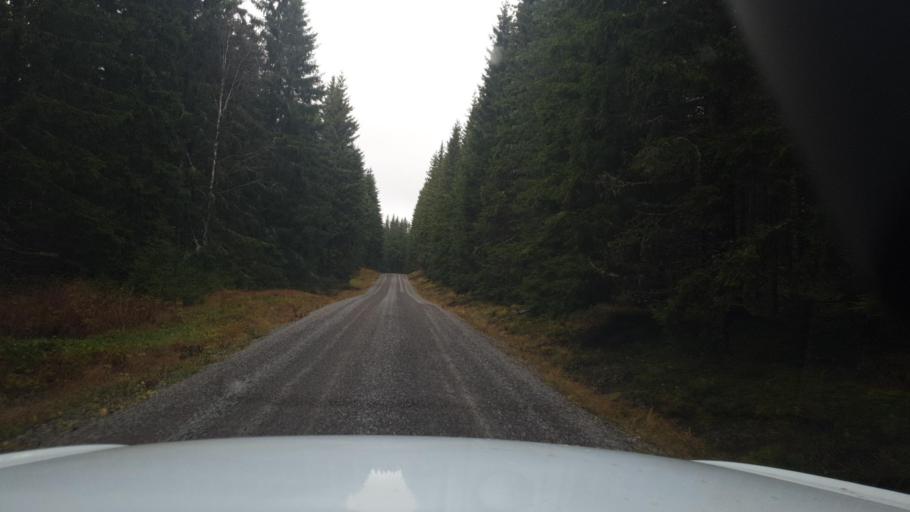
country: SE
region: Vaermland
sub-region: Eda Kommun
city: Charlottenberg
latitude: 60.0365
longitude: 12.6304
